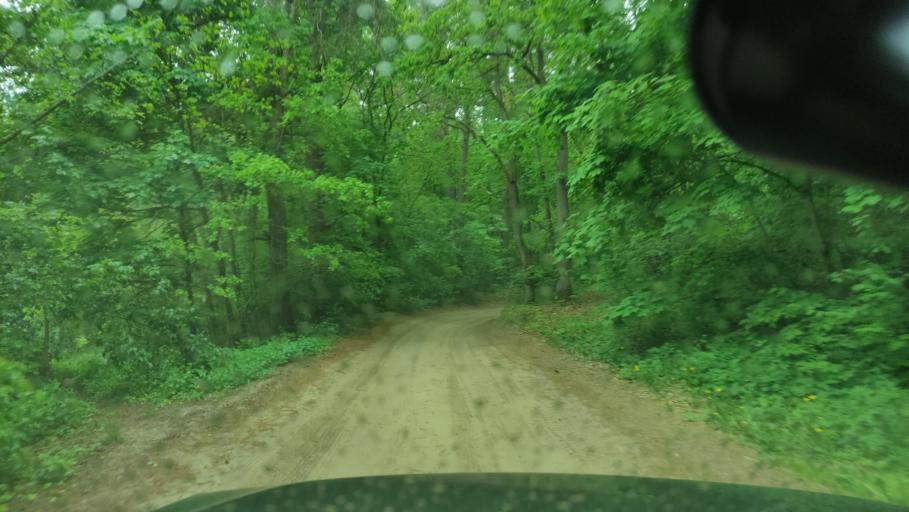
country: PL
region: Warmian-Masurian Voivodeship
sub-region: Powiat olsztynski
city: Olsztyn
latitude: 53.7605
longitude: 20.5221
